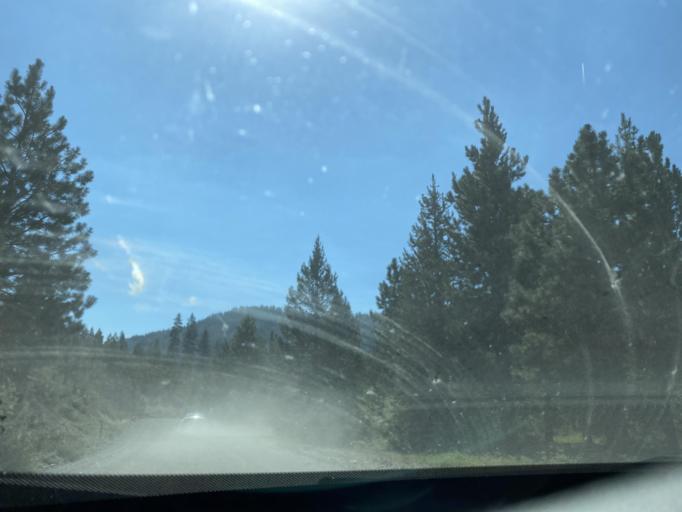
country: US
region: Oregon
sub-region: Deschutes County
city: Deschutes River Woods
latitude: 44.0338
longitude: -121.5251
